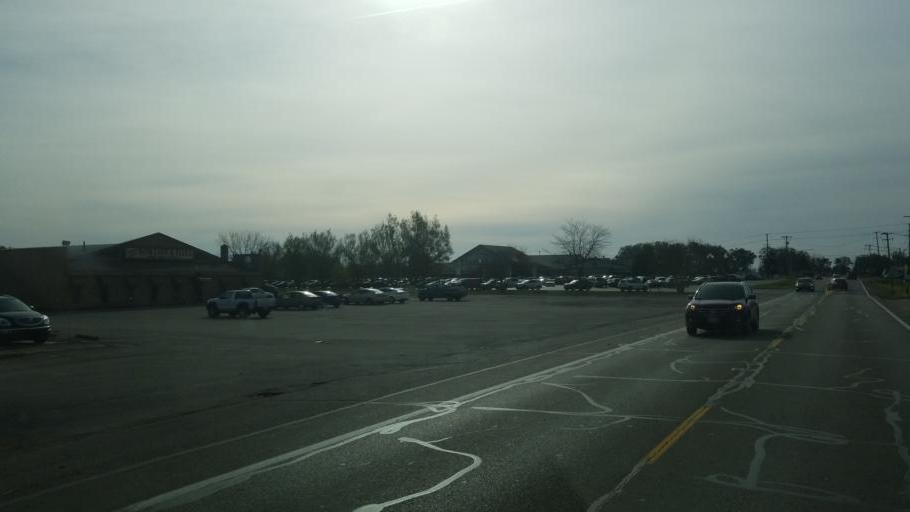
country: US
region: Ohio
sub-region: Madison County
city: Plain City
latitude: 40.1069
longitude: -83.2786
